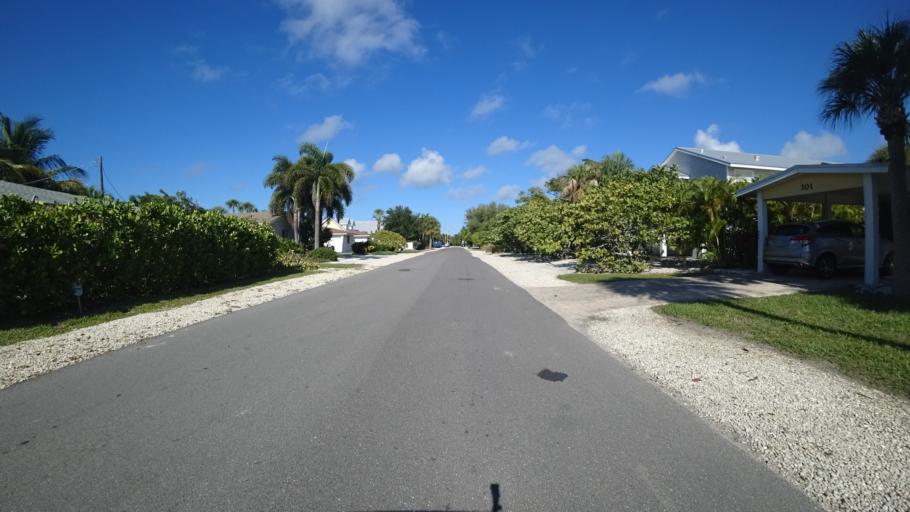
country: US
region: Florida
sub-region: Manatee County
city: Anna Maria
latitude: 27.5266
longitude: -82.7333
